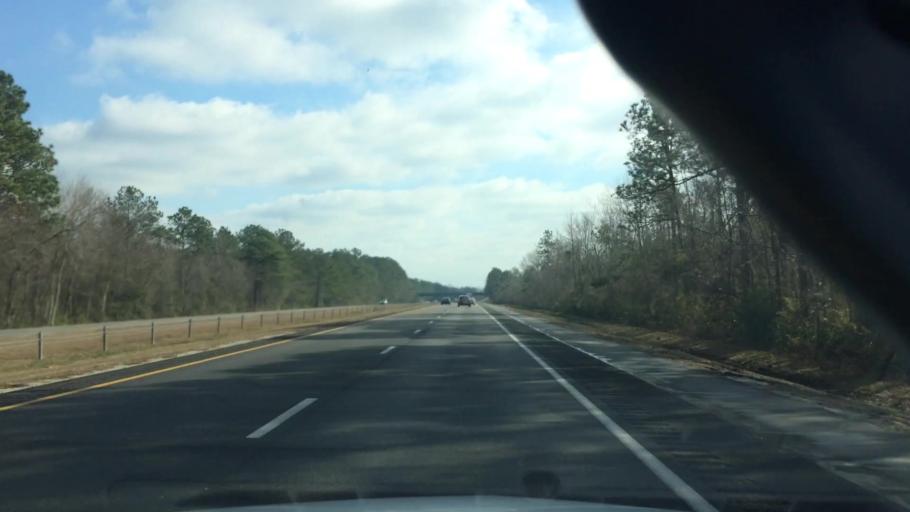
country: US
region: North Carolina
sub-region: Pender County
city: Burgaw
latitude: 34.6168
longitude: -77.9255
